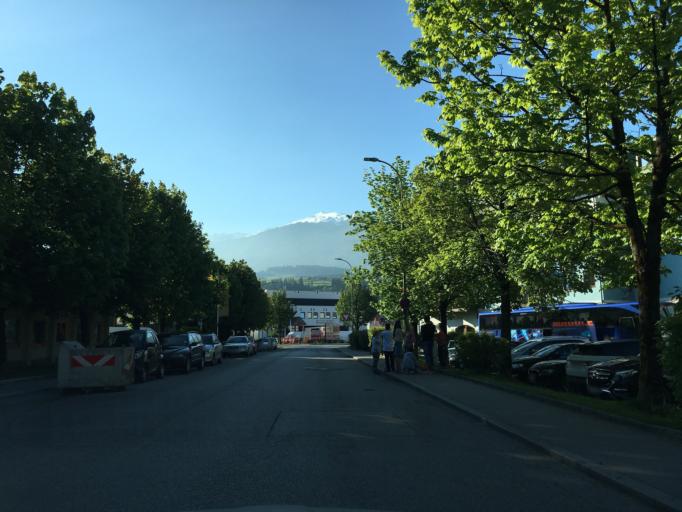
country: AT
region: Tyrol
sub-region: Politischer Bezirk Innsbruck Land
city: Ampass
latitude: 47.2654
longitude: 11.4288
